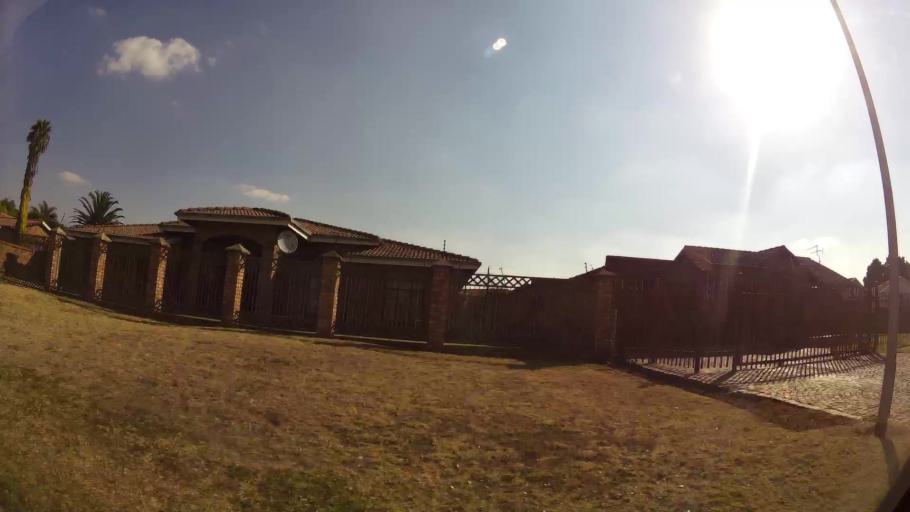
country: ZA
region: Gauteng
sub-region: Ekurhuleni Metropolitan Municipality
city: Brakpan
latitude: -26.2494
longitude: 28.3092
